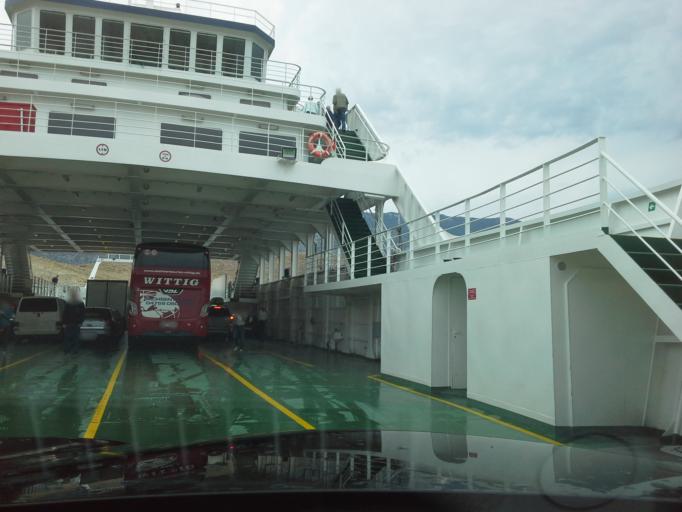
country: HR
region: Primorsko-Goranska
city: Banjol
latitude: 44.7063
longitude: 14.8608
